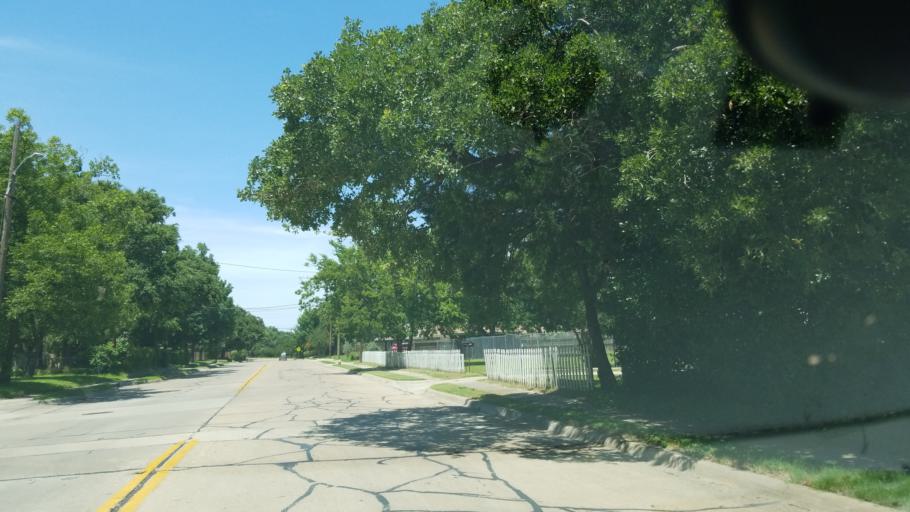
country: US
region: Texas
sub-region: Dallas County
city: Irving
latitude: 32.8202
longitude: -96.9256
